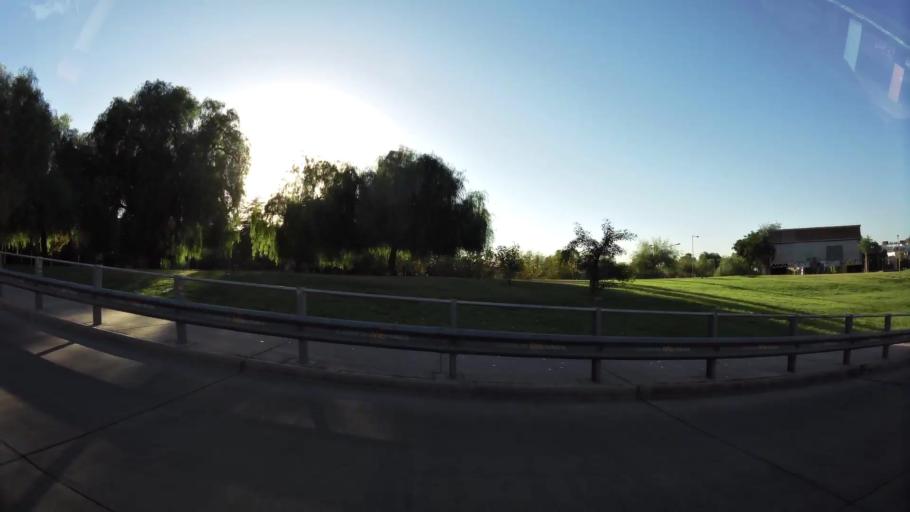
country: AR
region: Mendoza
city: Mendoza
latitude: -32.8757
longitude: -68.8407
